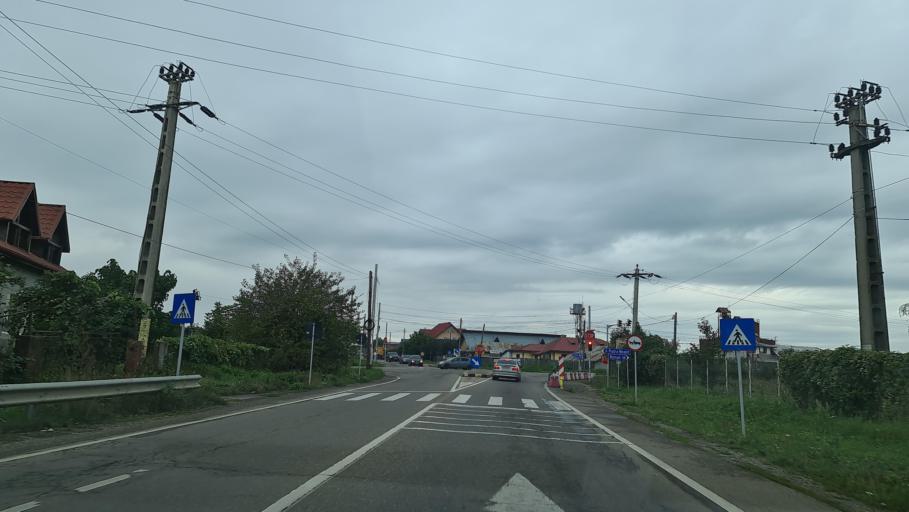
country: RO
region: Neamt
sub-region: Comuna Girov
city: Girov
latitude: 46.9492
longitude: 26.4891
